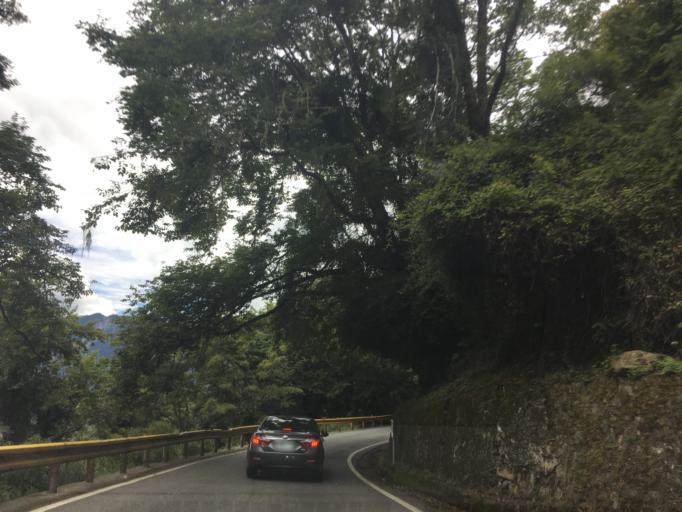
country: TW
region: Taiwan
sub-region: Hualien
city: Hualian
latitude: 24.1756
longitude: 121.3818
